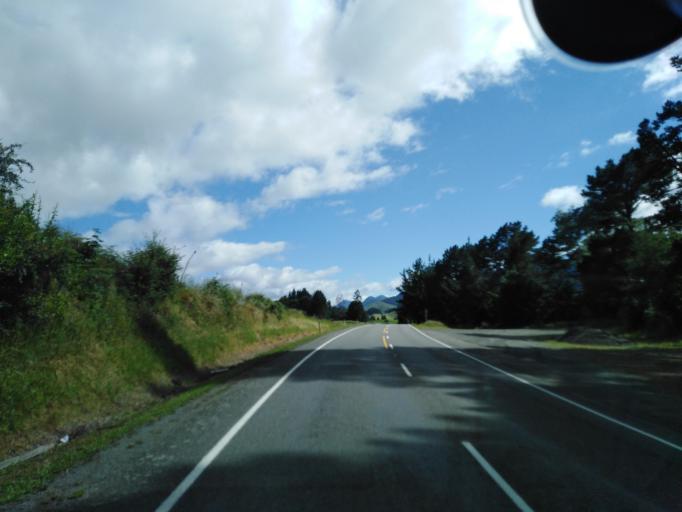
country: NZ
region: Nelson
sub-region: Nelson City
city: Nelson
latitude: -41.2846
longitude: 173.5720
